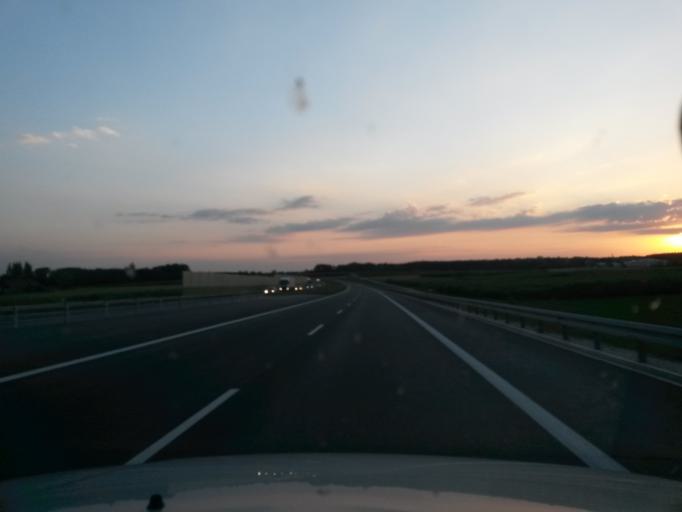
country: PL
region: Greater Poland Voivodeship
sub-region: Powiat kepinski
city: Kepno
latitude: 51.3173
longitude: 17.9875
